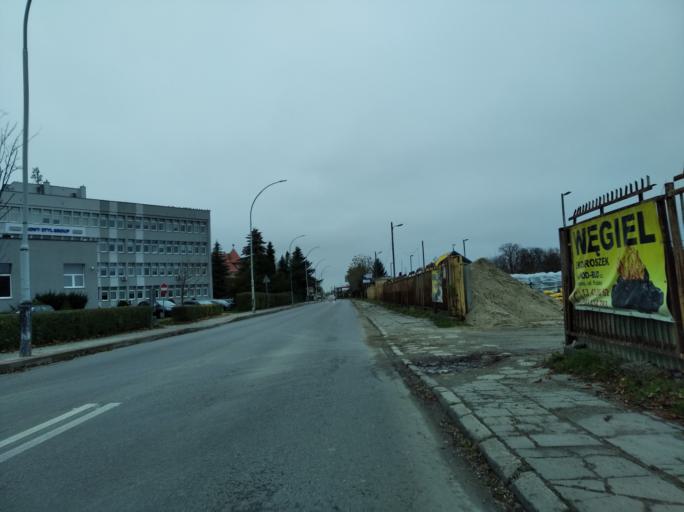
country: PL
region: Subcarpathian Voivodeship
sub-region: Krosno
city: Krosno
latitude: 49.6920
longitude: 21.7531
